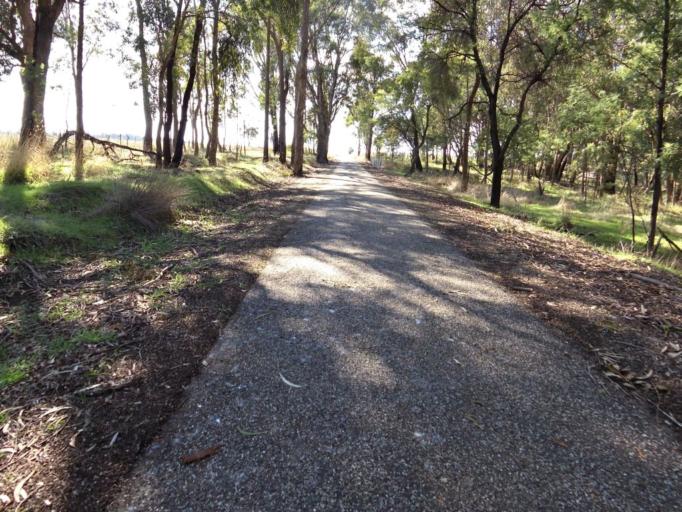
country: AU
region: Victoria
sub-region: Wangaratta
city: Wangaratta
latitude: -36.3994
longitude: 146.6478
